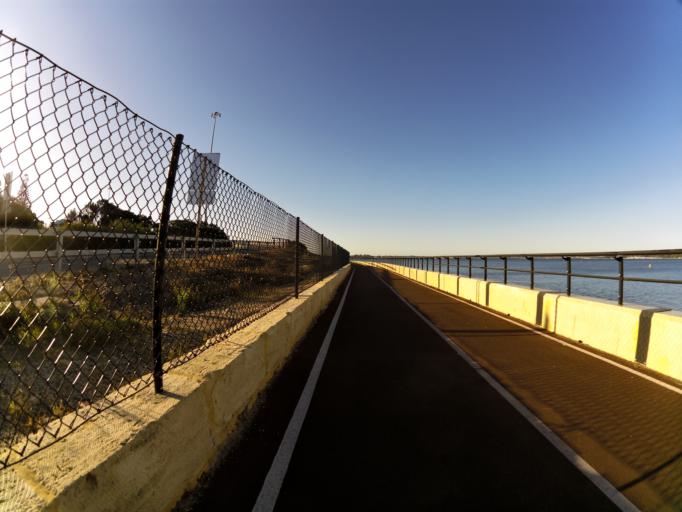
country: AU
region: Western Australia
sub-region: South Perth
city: South Perth
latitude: -31.9717
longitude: 115.8470
